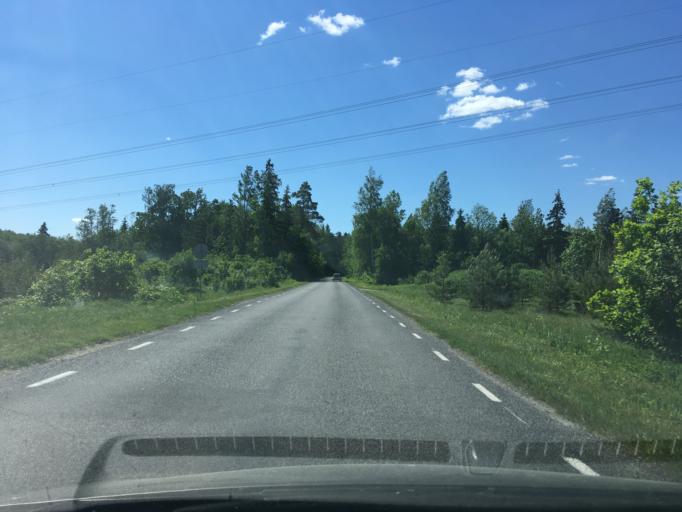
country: EE
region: Raplamaa
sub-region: Kohila vald
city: Kohila
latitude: 59.1199
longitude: 24.8355
